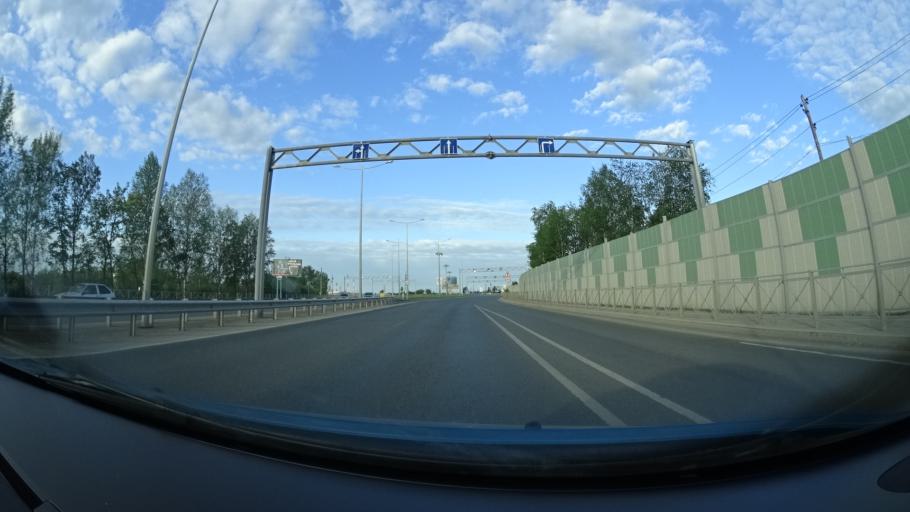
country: RU
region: Perm
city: Kultayevo
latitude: 57.9249
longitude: 56.0133
